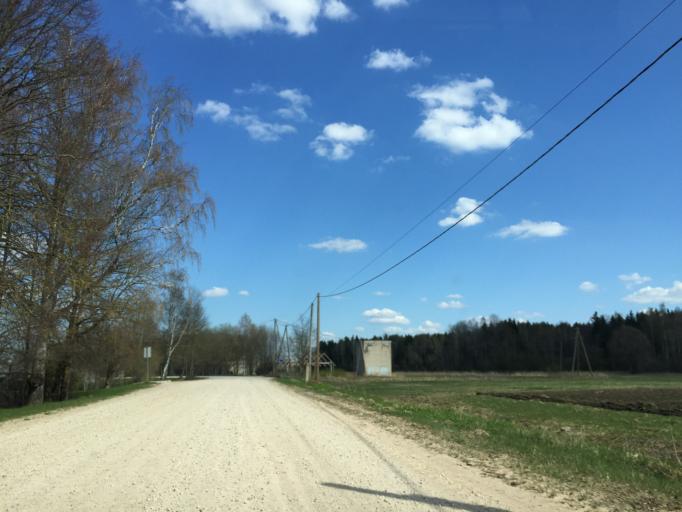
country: LV
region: Saulkrastu
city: Saulkrasti
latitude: 57.2539
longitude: 24.5339
